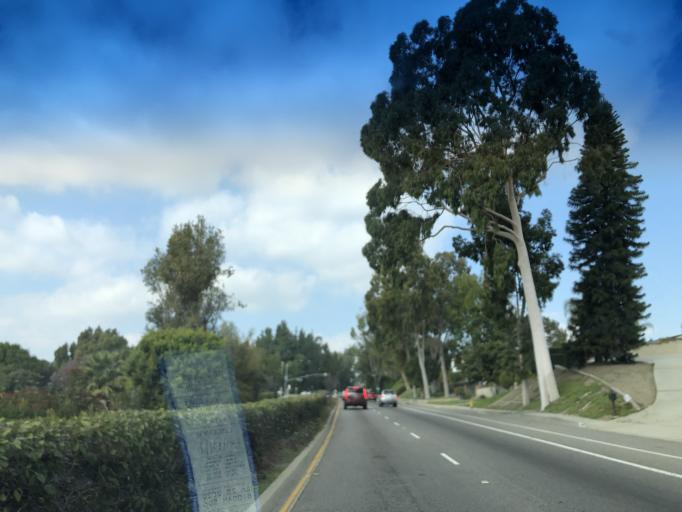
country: US
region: California
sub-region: Los Angeles County
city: Whittier
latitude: 33.9600
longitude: -118.0012
